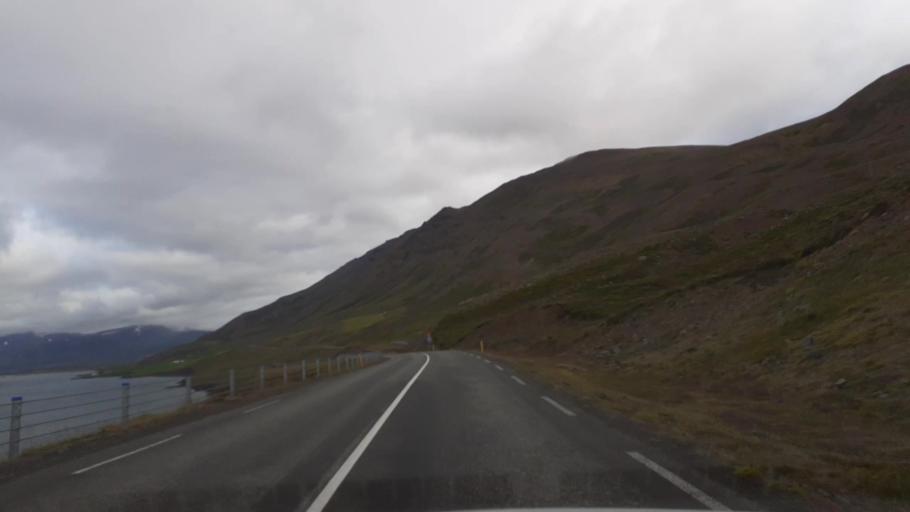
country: IS
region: Northeast
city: Akureyri
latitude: 65.8297
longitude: -18.0579
